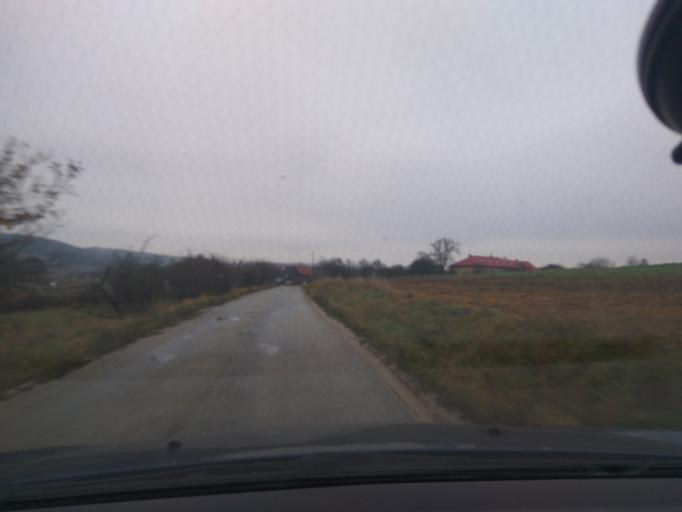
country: SK
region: Trnavsky
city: Vrbove
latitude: 48.6815
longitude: 17.6766
